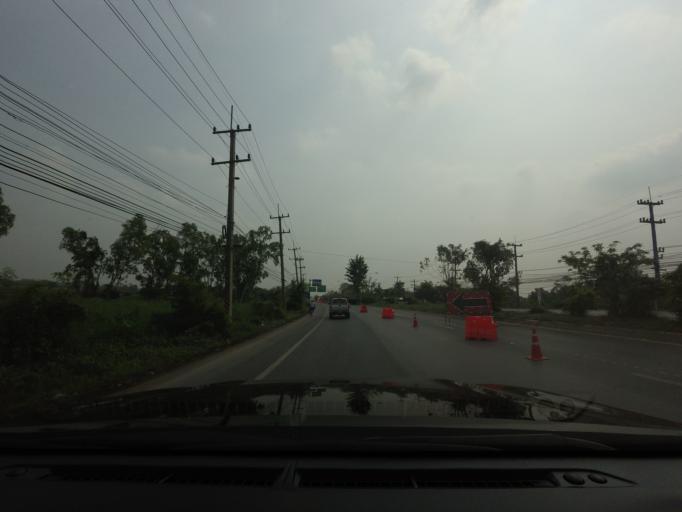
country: TH
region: Nakhon Nayok
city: Nakhon Nayok
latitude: 14.1924
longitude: 101.2250
